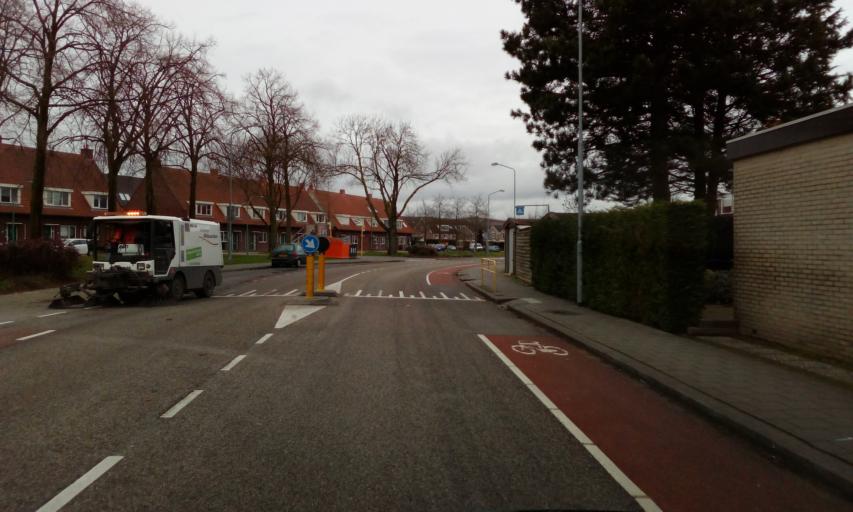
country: NL
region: South Holland
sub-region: Gemeente Alblasserdam
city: Alblasserdam
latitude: 51.8731
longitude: 4.6401
